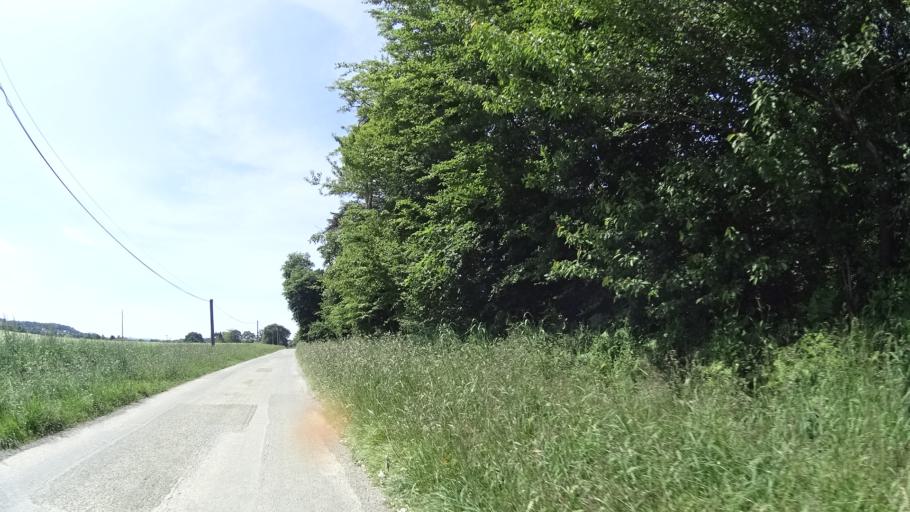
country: FR
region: Brittany
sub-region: Departement d'Ille-et-Vilaine
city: Iffendic
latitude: 48.1241
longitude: -2.0195
